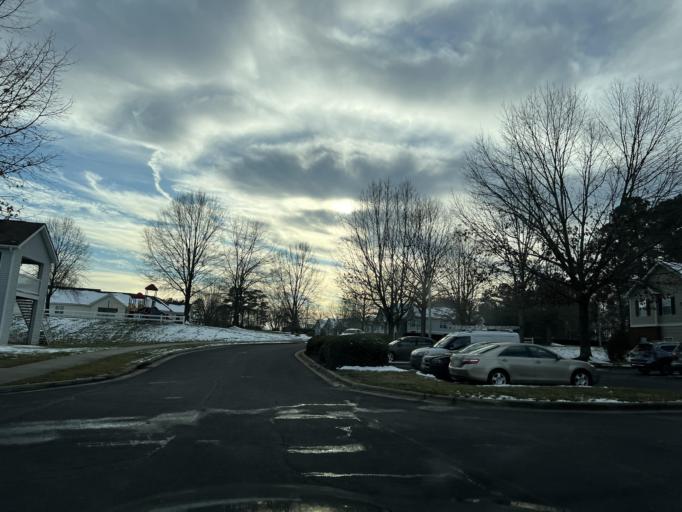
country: US
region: North Carolina
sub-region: Wake County
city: Raleigh
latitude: 35.8716
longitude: -78.5875
